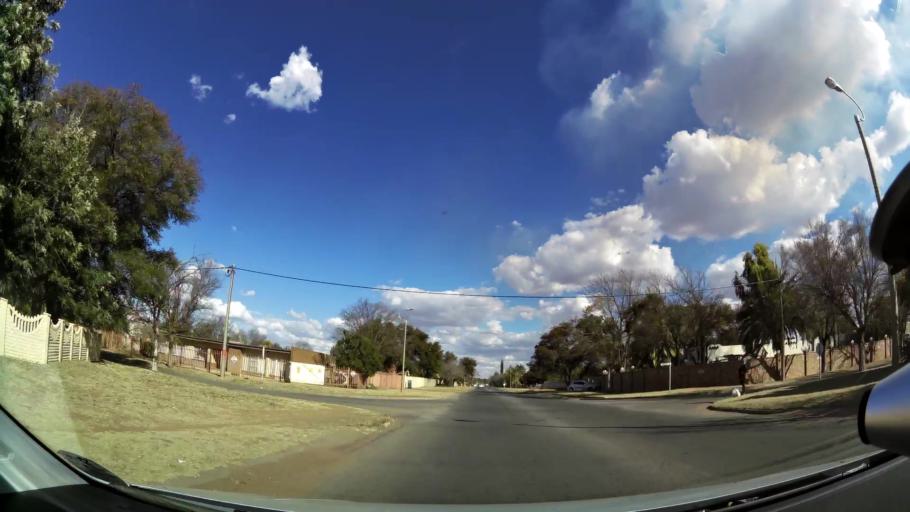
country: ZA
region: North-West
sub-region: Dr Kenneth Kaunda District Municipality
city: Klerksdorp
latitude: -26.8317
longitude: 26.6567
